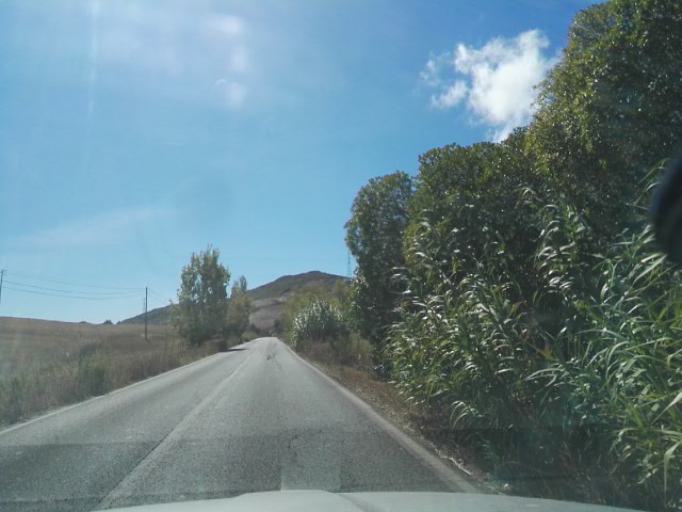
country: PT
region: Lisbon
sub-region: Arruda Dos Vinhos
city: Arruda dos Vinhos
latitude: 38.9508
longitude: -9.0574
